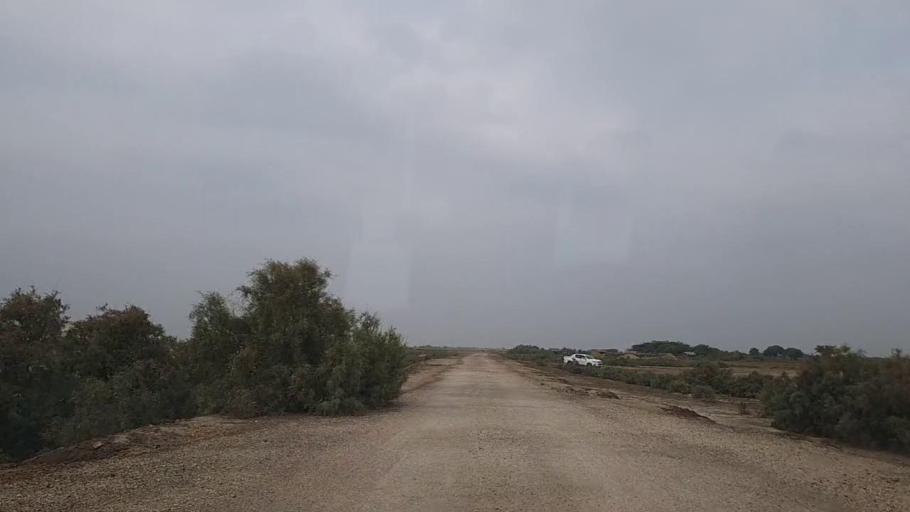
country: PK
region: Sindh
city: Mirpur Sakro
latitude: 24.6240
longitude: 67.7183
